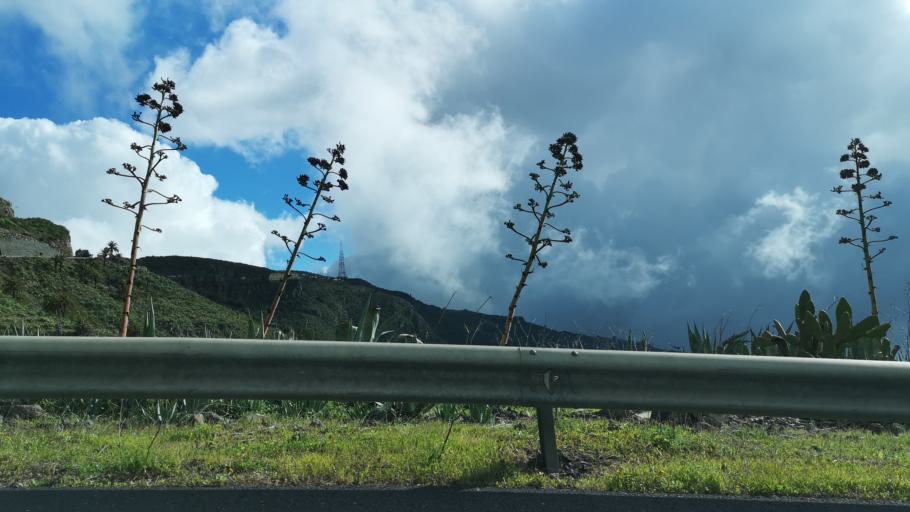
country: ES
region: Canary Islands
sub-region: Provincia de Santa Cruz de Tenerife
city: Alajero
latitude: 28.0966
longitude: -17.1905
